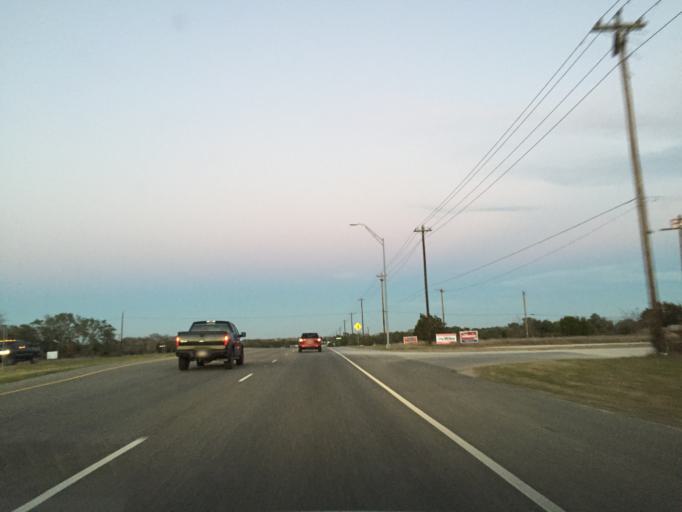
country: US
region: Texas
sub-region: Travis County
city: Jonestown
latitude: 30.5125
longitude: -97.8798
